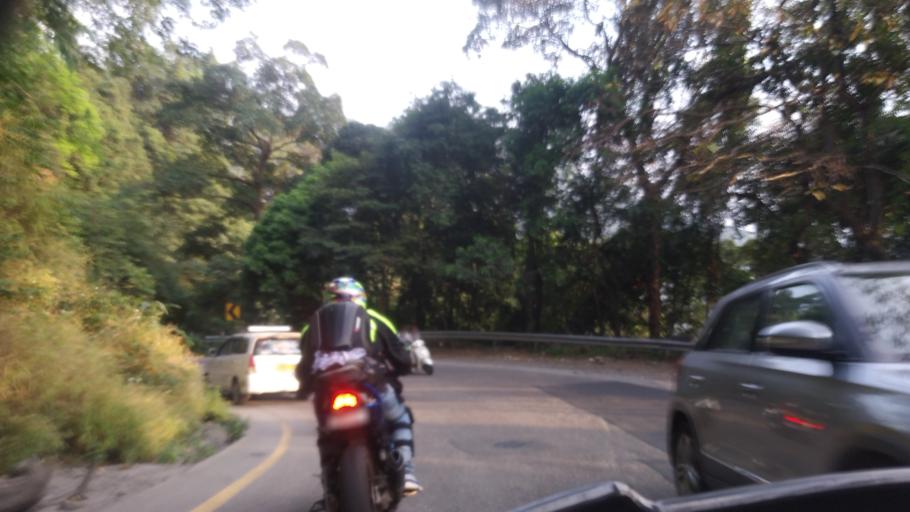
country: IN
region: Kerala
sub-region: Wayanad
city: Kalpetta
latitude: 11.5099
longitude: 76.0248
